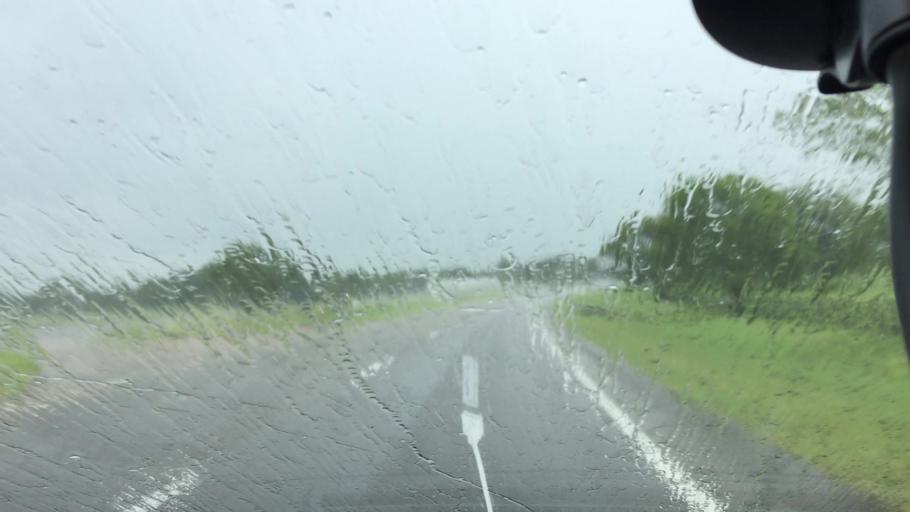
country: US
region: Alabama
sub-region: Montgomery County
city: Pike Road
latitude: 32.2263
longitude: -86.1185
